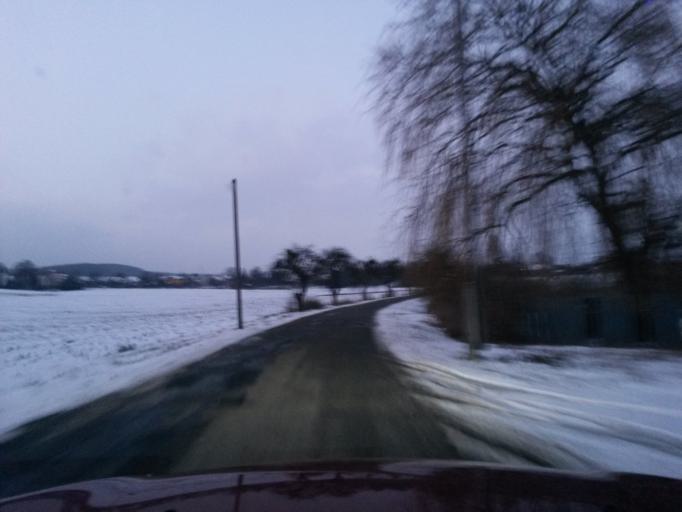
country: SK
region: Kosicky
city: Kosice
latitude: 48.7423
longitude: 21.3233
